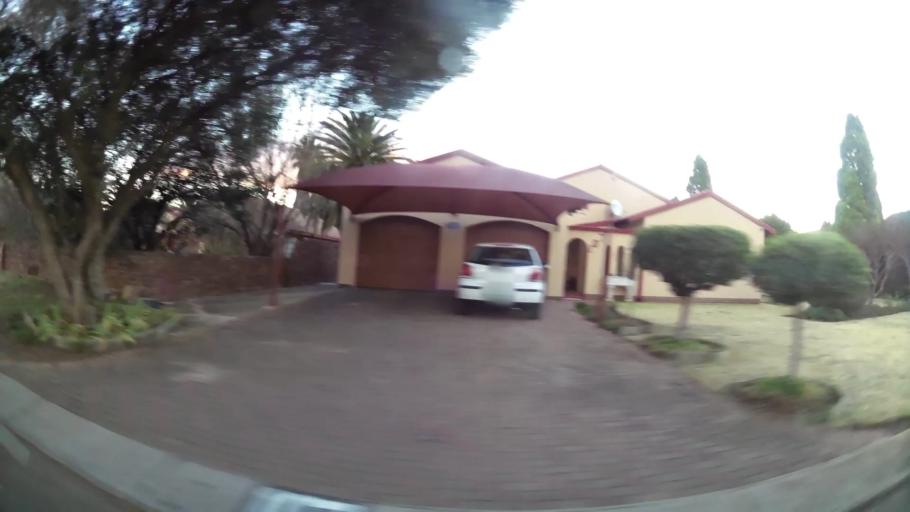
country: ZA
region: North-West
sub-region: Dr Kenneth Kaunda District Municipality
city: Potchefstroom
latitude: -26.7174
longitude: 27.1233
